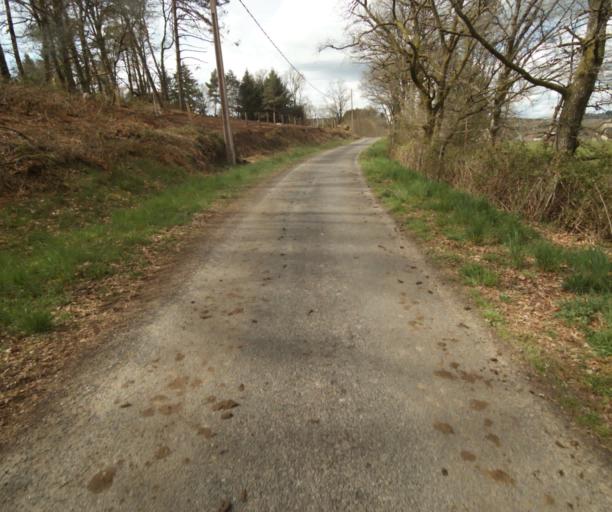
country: FR
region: Limousin
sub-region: Departement de la Correze
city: Correze
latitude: 45.3789
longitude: 1.9044
